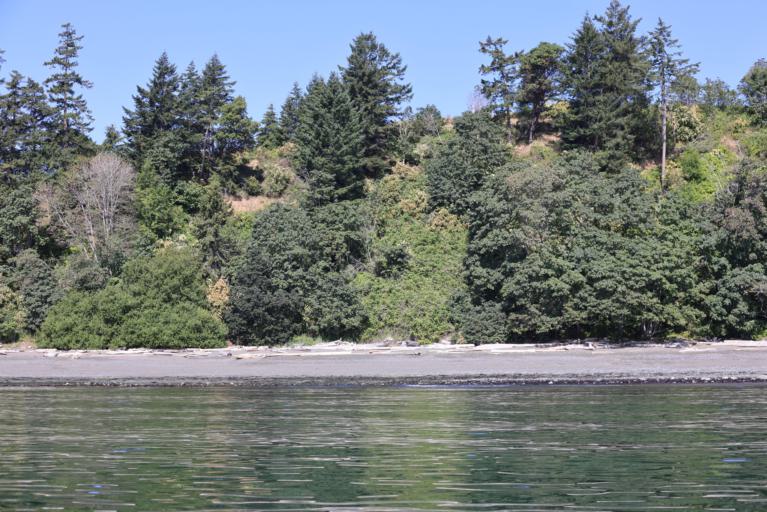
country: CA
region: British Columbia
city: Colwood
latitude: 48.4023
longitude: -123.4825
